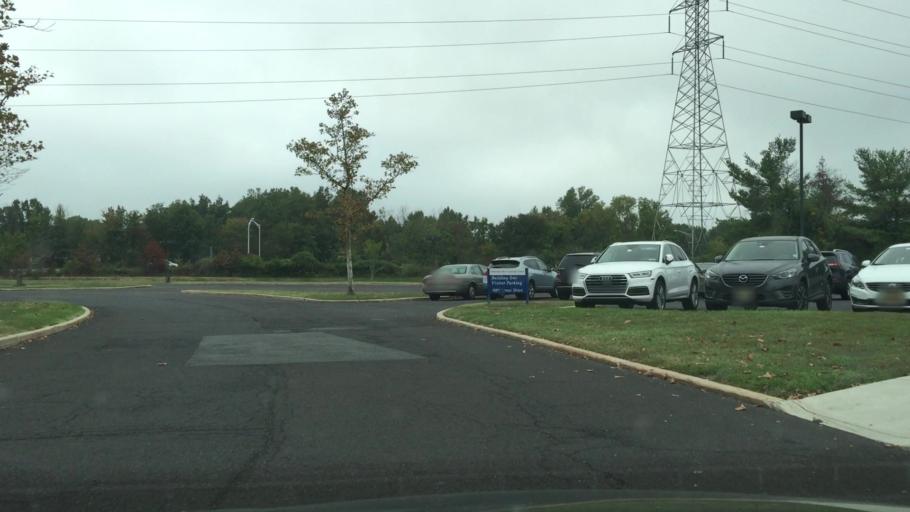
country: US
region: New Jersey
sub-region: Mercer County
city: Lawrenceville
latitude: 40.2877
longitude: -74.7099
